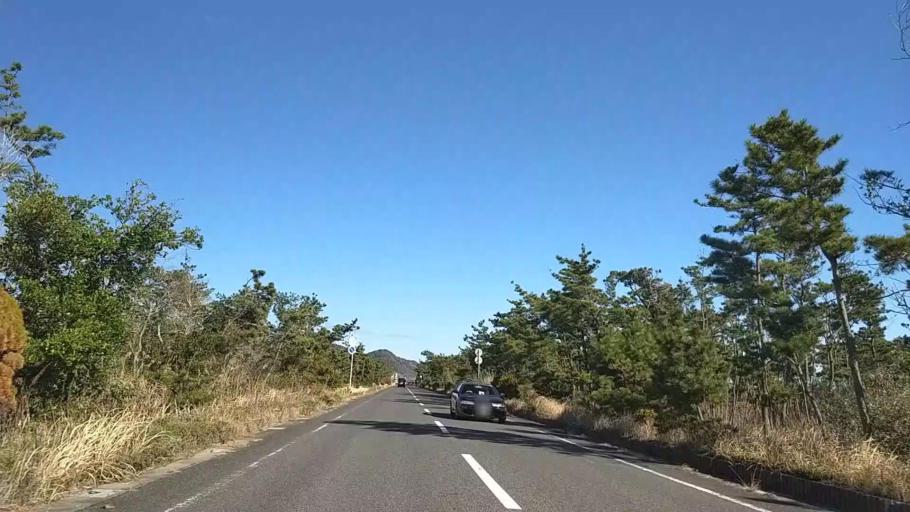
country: JP
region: Chiba
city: Tateyama
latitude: 35.0164
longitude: 139.9844
